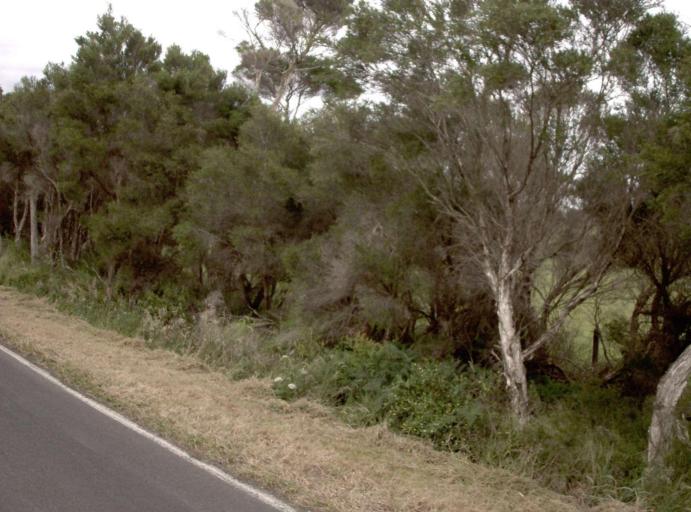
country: AU
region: Victoria
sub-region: Bass Coast
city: North Wonthaggi
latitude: -38.5578
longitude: 145.6371
